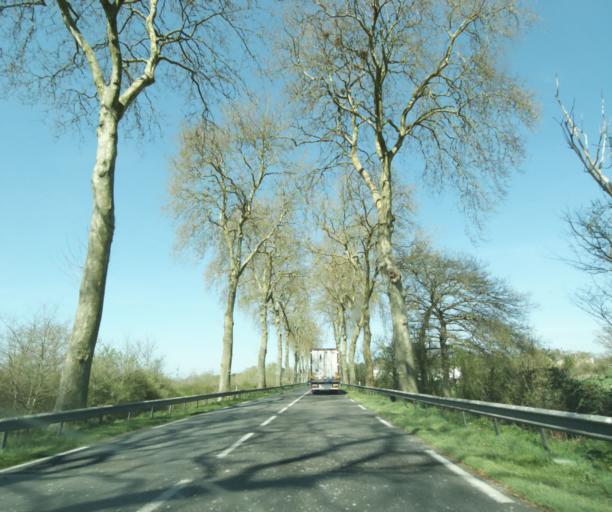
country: FR
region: Bourgogne
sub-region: Departement de la Nievre
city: Chantenay-Saint-Imbert
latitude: 46.7239
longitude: 3.1785
